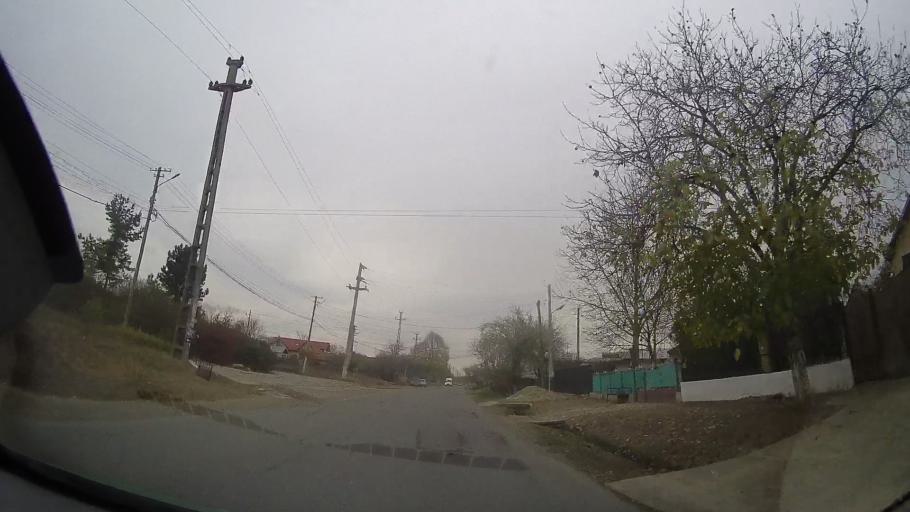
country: RO
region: Prahova
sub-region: Oras Urlati
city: Urlati
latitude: 45.0016
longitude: 26.2274
